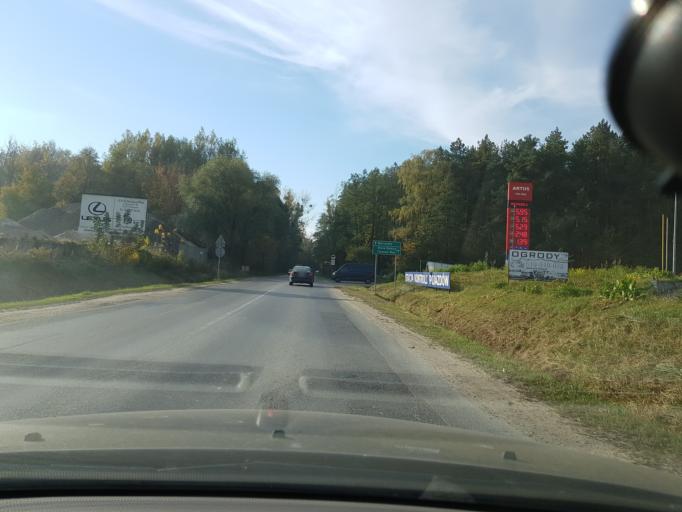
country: PL
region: Masovian Voivodeship
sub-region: Powiat warszawski zachodni
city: Babice
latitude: 52.2756
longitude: 20.8753
